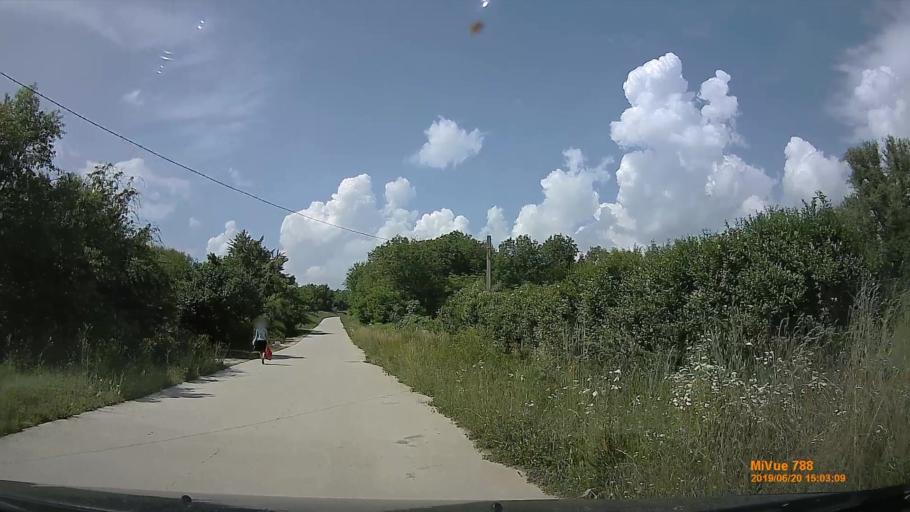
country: HU
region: Baranya
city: Kozarmisleny
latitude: 45.9862
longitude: 18.2624
